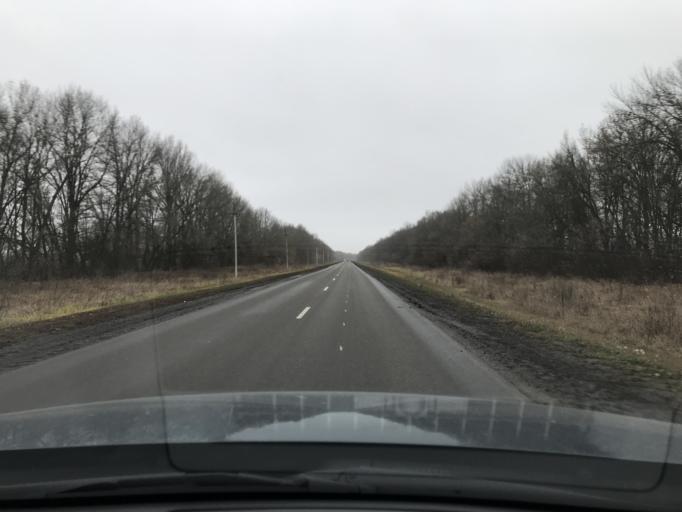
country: RU
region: Penza
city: Zemetchino
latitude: 53.5338
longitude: 42.6604
